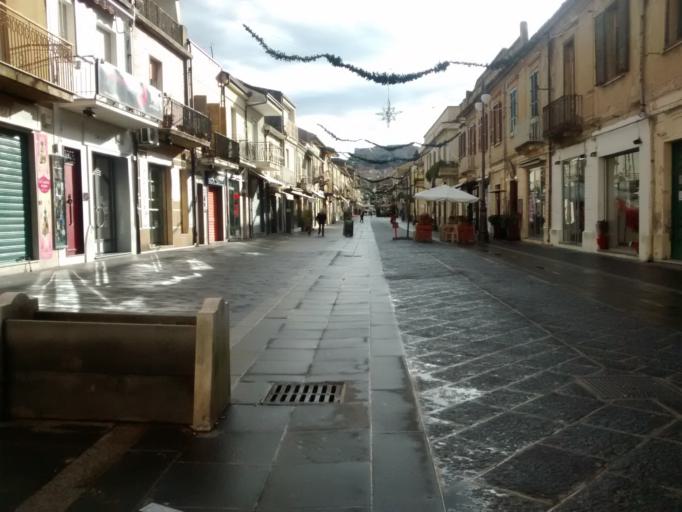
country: IT
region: Calabria
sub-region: Provincia di Vibo-Valentia
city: Vibo Valentia
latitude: 38.6745
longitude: 16.0991
